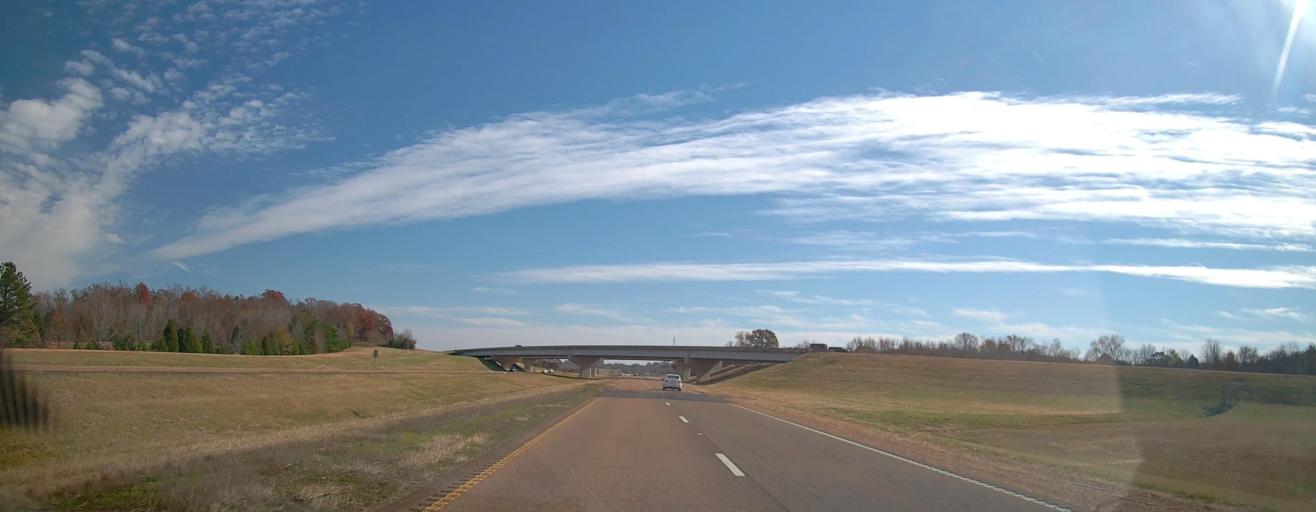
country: US
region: Tennessee
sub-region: Fayette County
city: Piperton
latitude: 34.9666
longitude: -89.5464
